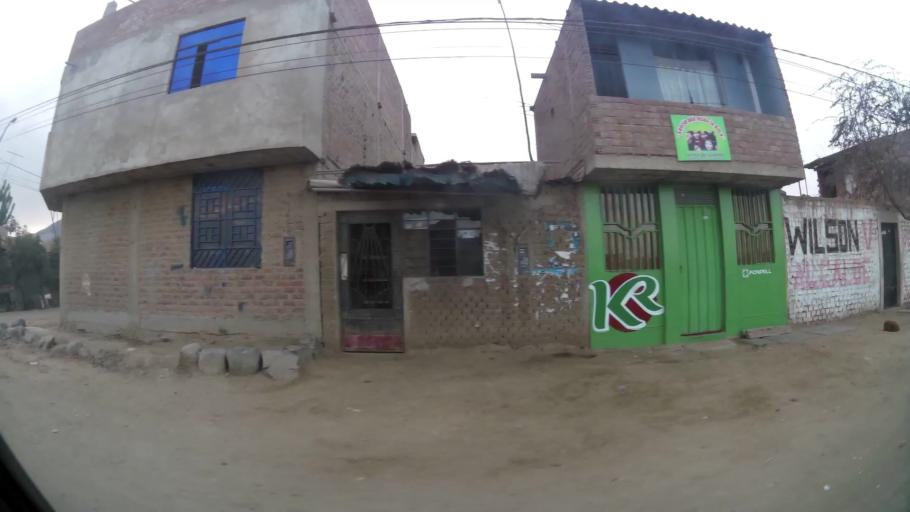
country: PE
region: La Libertad
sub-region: Provincia de Trujillo
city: El Porvenir
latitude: -8.0664
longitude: -79.0165
